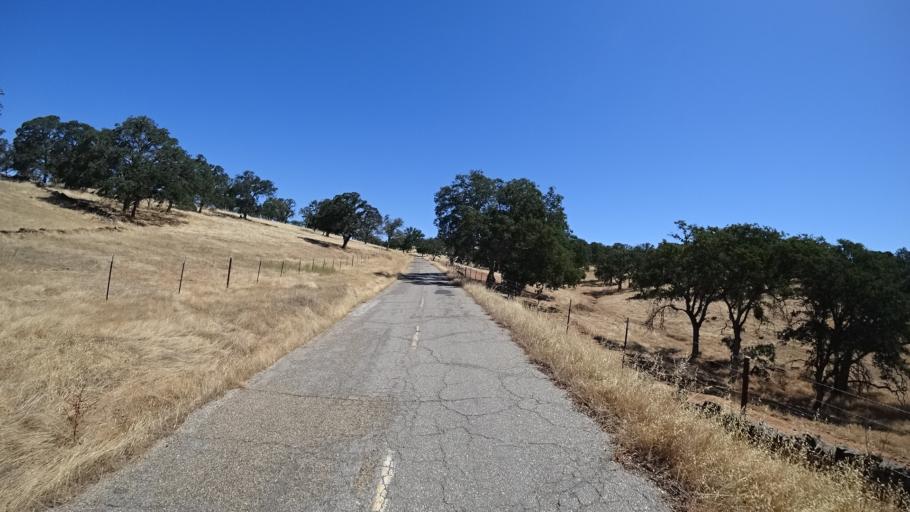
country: US
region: California
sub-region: Calaveras County
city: Copperopolis
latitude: 37.9357
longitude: -120.7352
